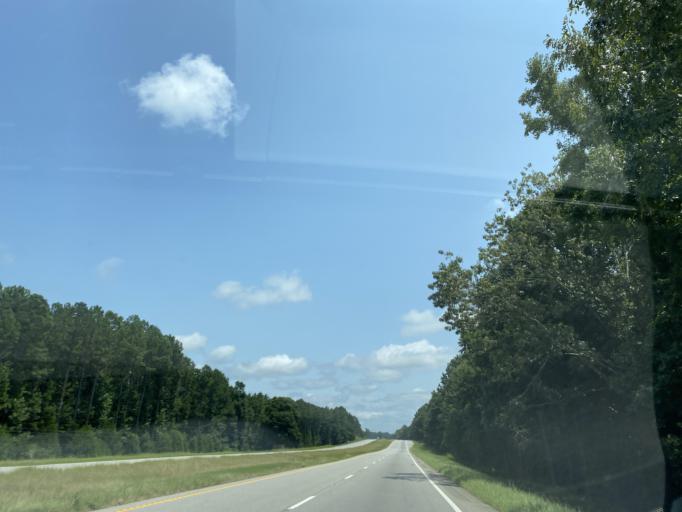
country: US
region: Georgia
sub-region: Telfair County
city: Lumber City
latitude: 31.9059
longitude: -82.6587
